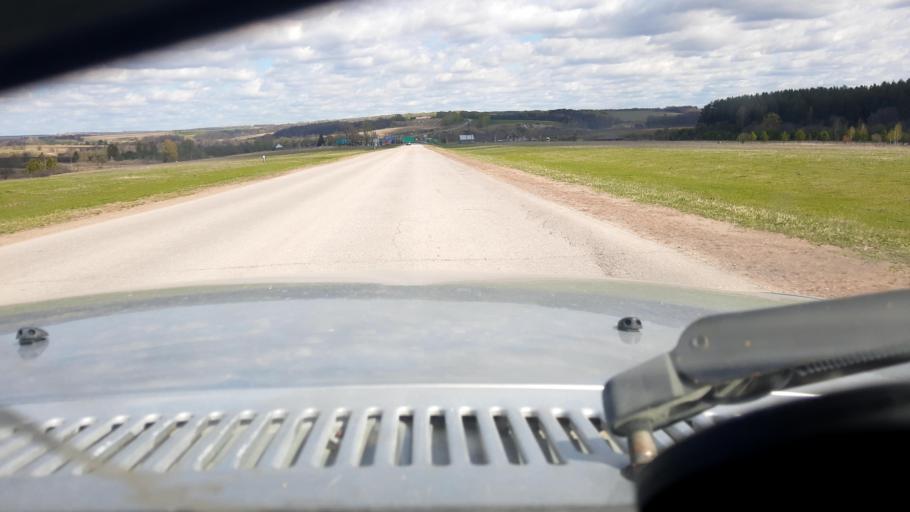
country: RU
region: Bashkortostan
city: Yazykovo
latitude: 55.1217
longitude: 56.0709
